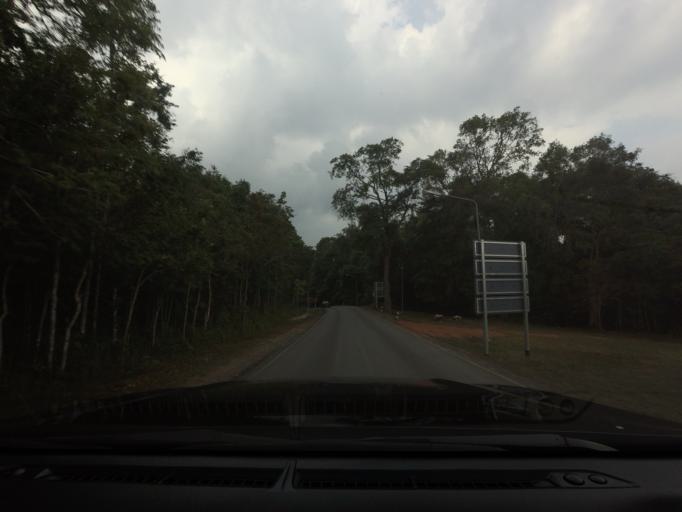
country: TH
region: Nakhon Ratchasima
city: Pak Chong
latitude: 14.4342
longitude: 101.3720
